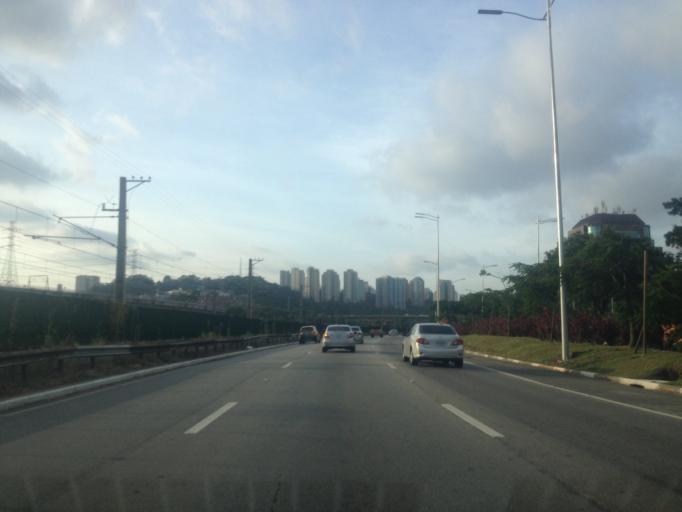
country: BR
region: Sao Paulo
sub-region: Taboao Da Serra
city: Taboao da Serra
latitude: -23.6495
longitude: -46.7248
